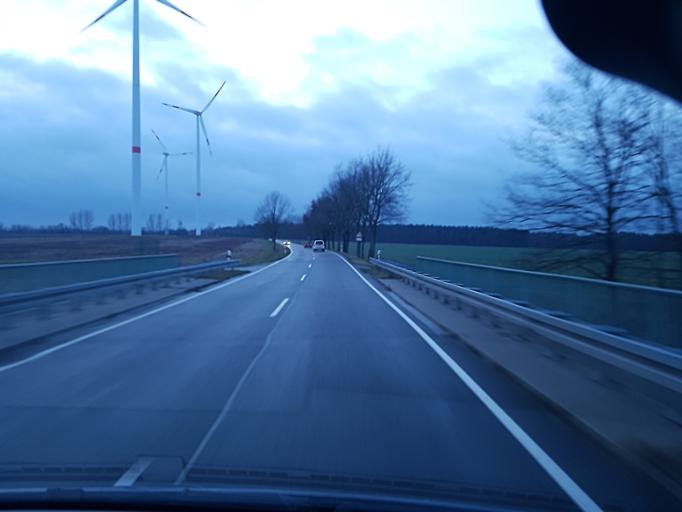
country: DE
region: Brandenburg
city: Bronkow
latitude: 51.6503
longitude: 13.8815
